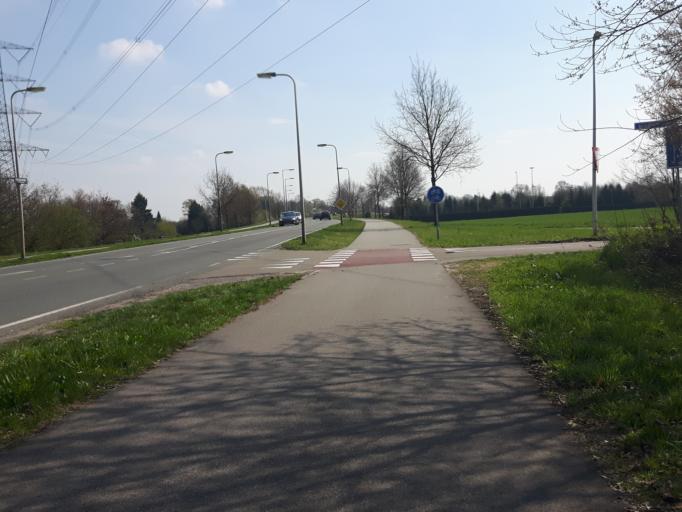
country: NL
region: Overijssel
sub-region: Gemeente Enschede
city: Enschede
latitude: 52.2047
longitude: 6.8549
